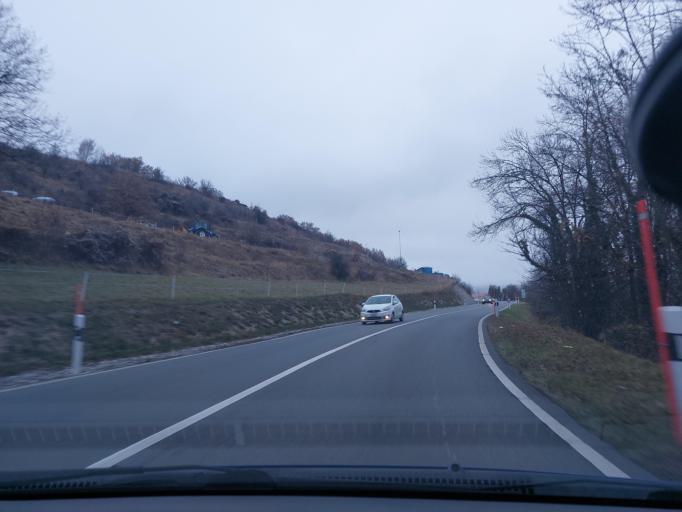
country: CH
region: Valais
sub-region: Sion District
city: Grimisuat
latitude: 46.2663
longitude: 7.3972
